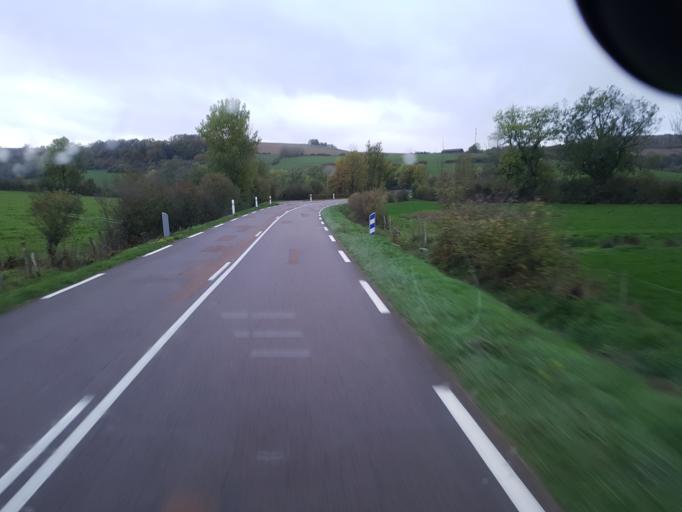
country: FR
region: Bourgogne
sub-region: Departement de la Cote-d'Or
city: Chatillon-sur-Seine
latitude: 47.6969
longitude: 4.6178
